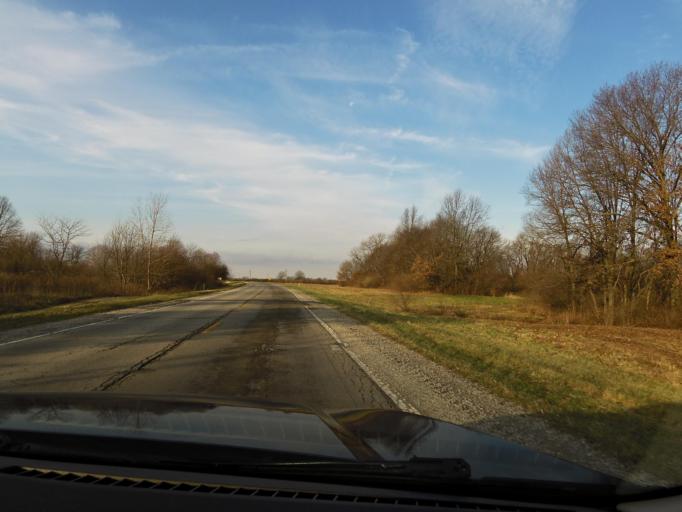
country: US
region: Illinois
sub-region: Bond County
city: Greenville
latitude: 38.9185
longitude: -89.2794
